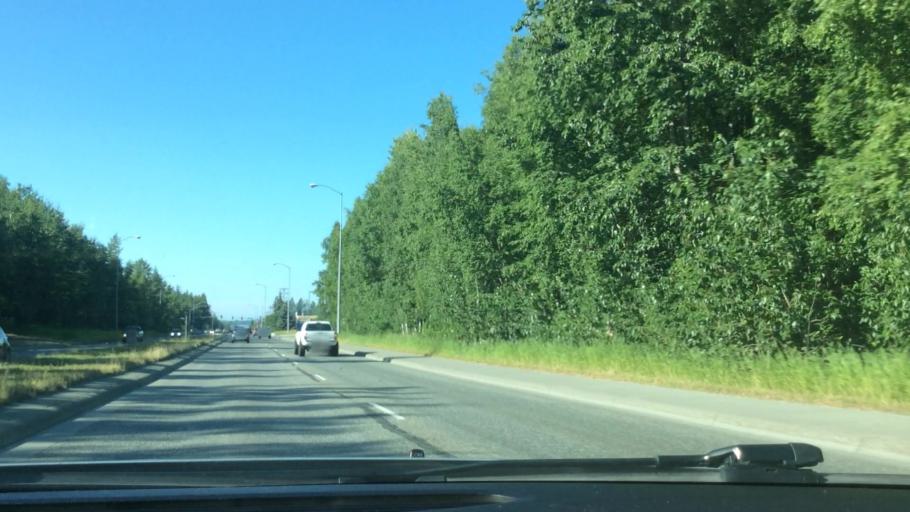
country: US
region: Alaska
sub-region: Anchorage Municipality
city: Anchorage
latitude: 61.2061
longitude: -149.7782
